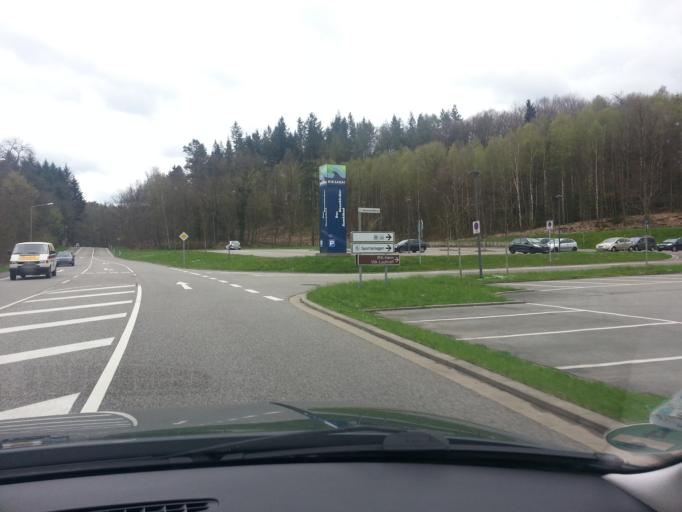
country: DE
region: Saarland
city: Neunkirchen
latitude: 49.3278
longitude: 7.2005
